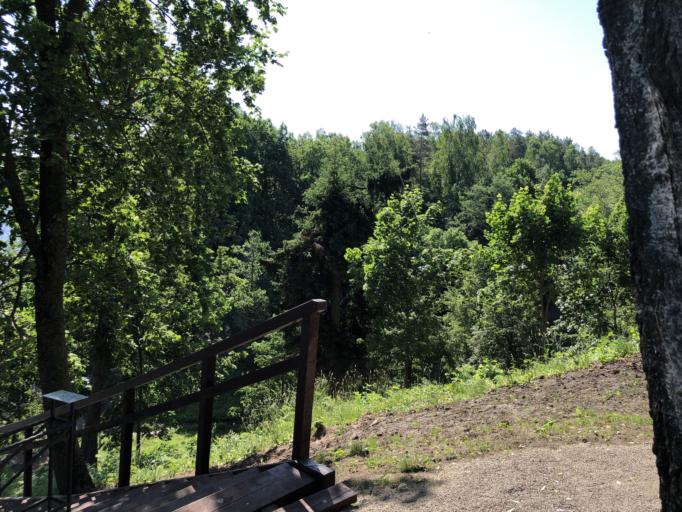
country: LT
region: Kauno apskritis
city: Dainava (Kaunas)
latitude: 54.8562
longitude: 24.0194
